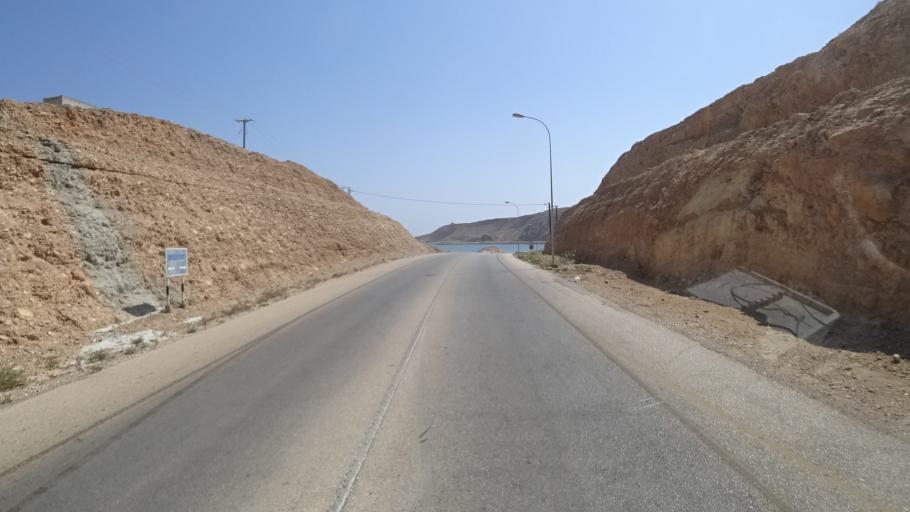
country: OM
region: Ash Sharqiyah
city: Sur
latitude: 22.5518
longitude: 59.5304
